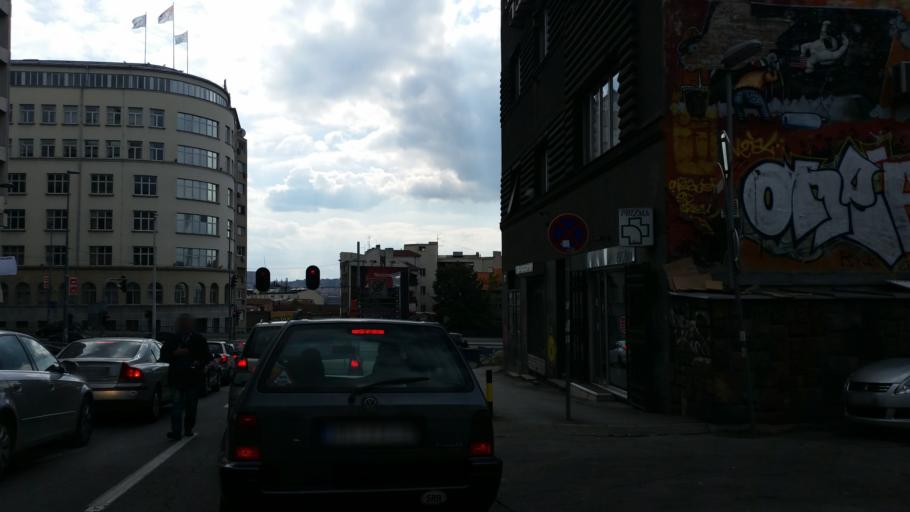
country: RS
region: Central Serbia
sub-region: Belgrade
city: Stari Grad
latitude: 44.8156
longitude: 20.4531
